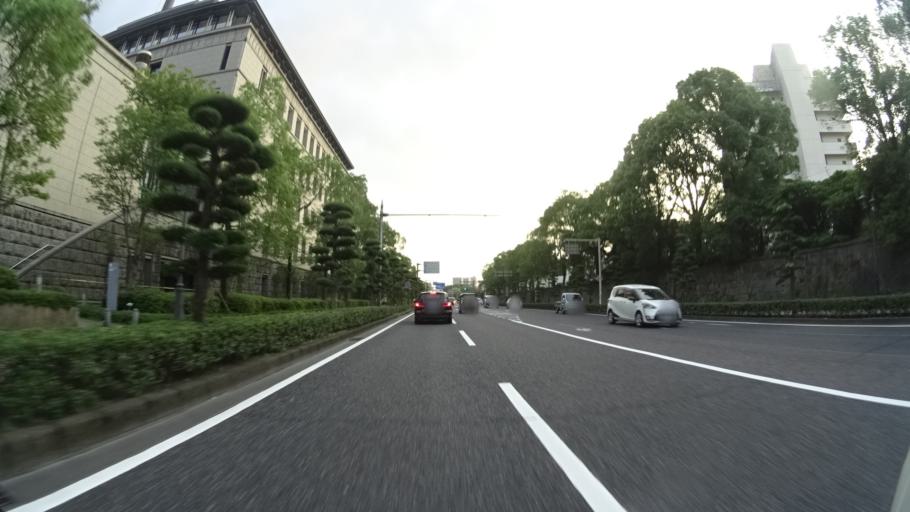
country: JP
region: Kagoshima
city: Kagoshima-shi
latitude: 31.6003
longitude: 130.5575
